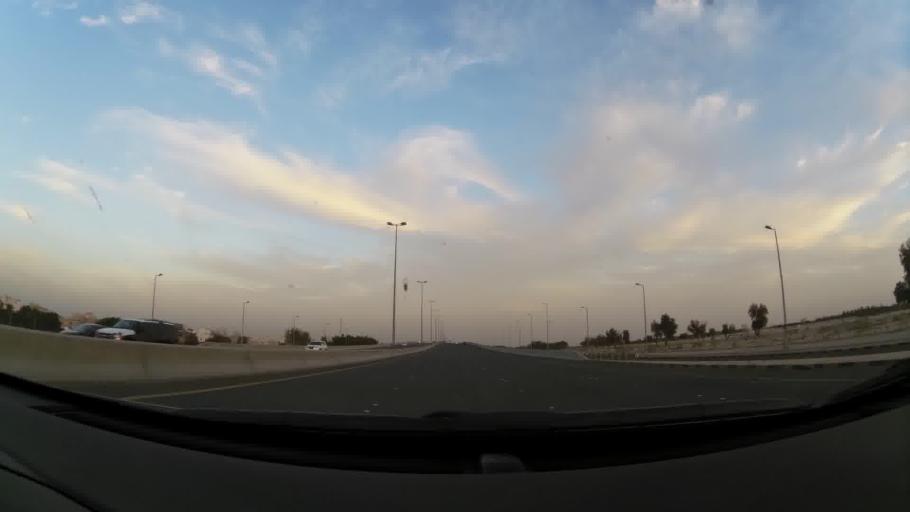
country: KW
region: Al Asimah
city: Ar Rabiyah
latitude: 29.3112
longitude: 47.8248
